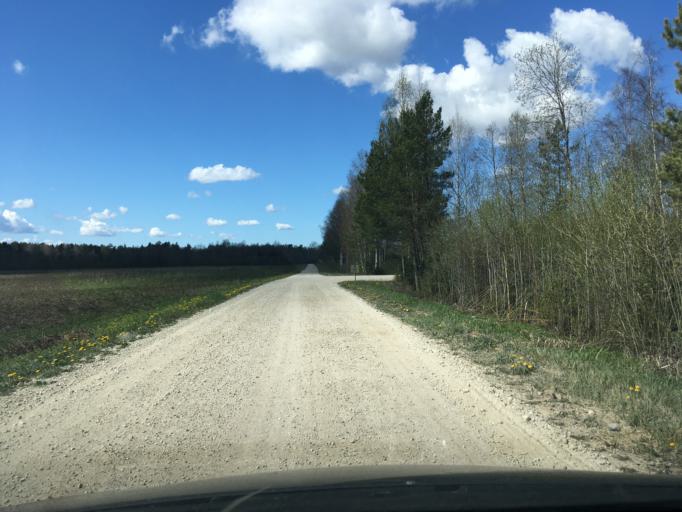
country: EE
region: Harju
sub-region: Raasiku vald
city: Raasiku
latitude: 59.2080
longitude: 25.1732
